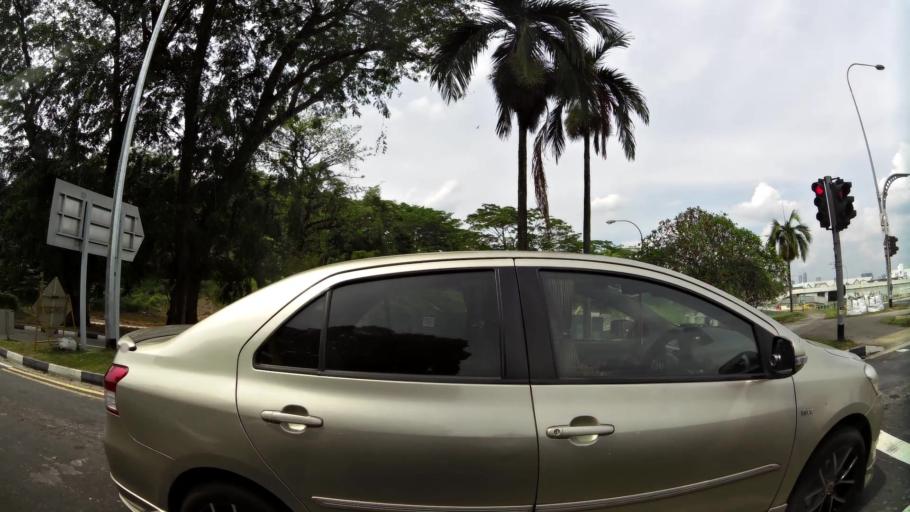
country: MY
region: Johor
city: Johor Bahru
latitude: 1.4235
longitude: 103.7569
